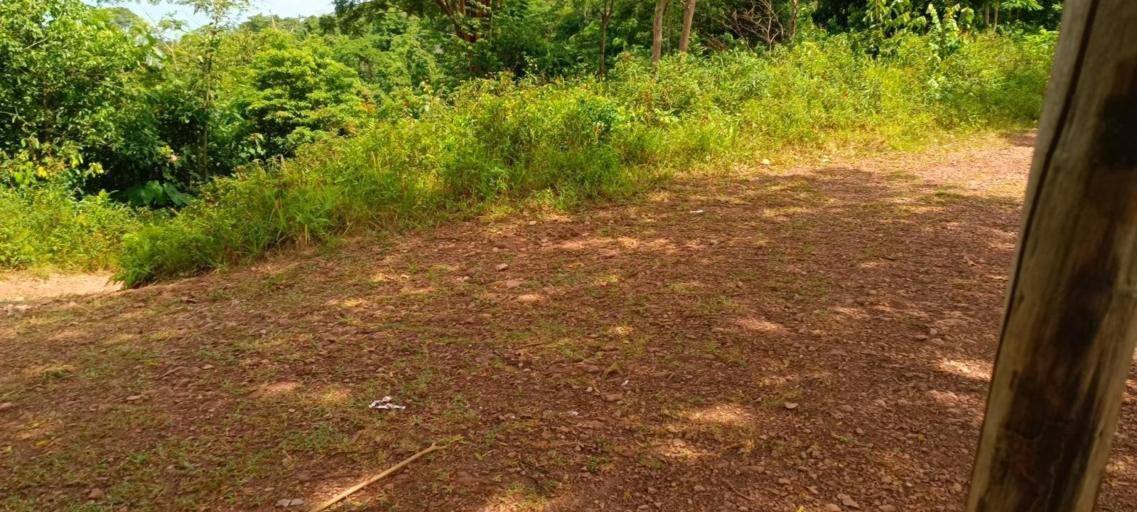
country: MY
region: Kedah
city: Sungai Petani
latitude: 5.5989
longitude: 100.4599
